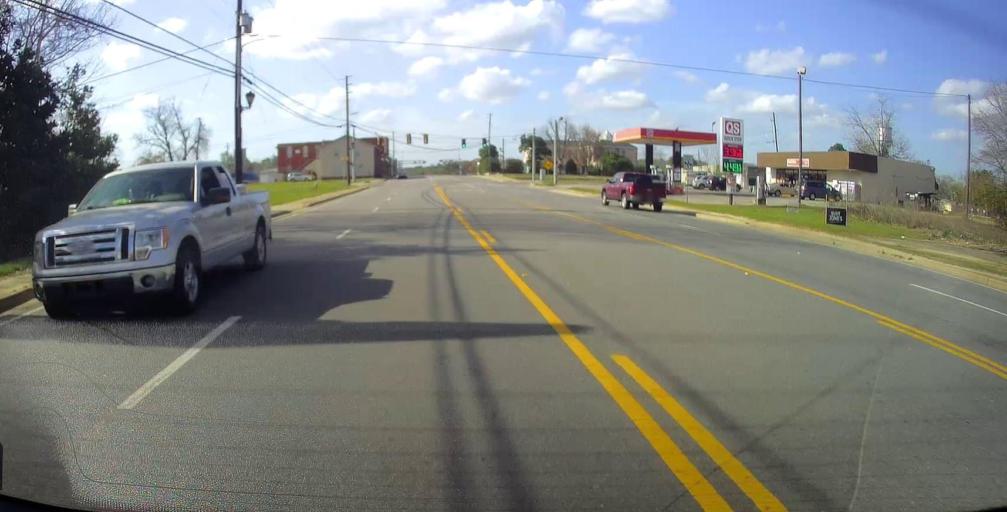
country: US
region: Georgia
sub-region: Telfair County
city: Helena
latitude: 32.0726
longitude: -82.9126
